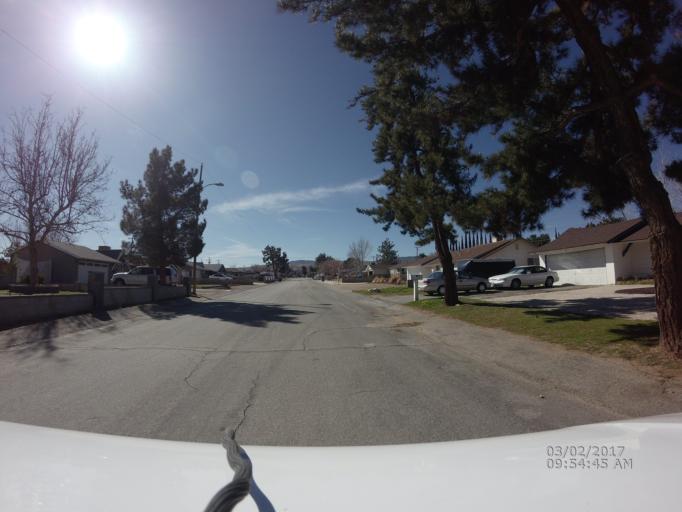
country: US
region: California
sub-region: Los Angeles County
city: Quartz Hill
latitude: 34.6396
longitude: -118.2143
